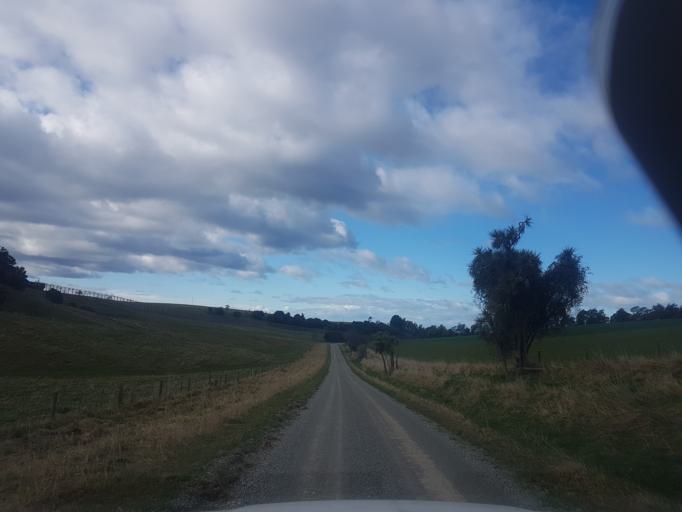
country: NZ
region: Canterbury
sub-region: Timaru District
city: Pleasant Point
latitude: -44.1839
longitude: 171.1365
